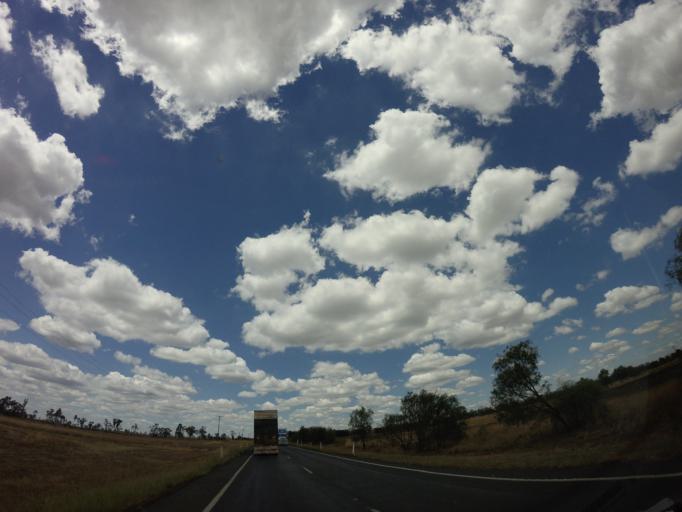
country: AU
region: Queensland
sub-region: Toowoomba
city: Oakey
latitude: -27.8350
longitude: 151.3437
